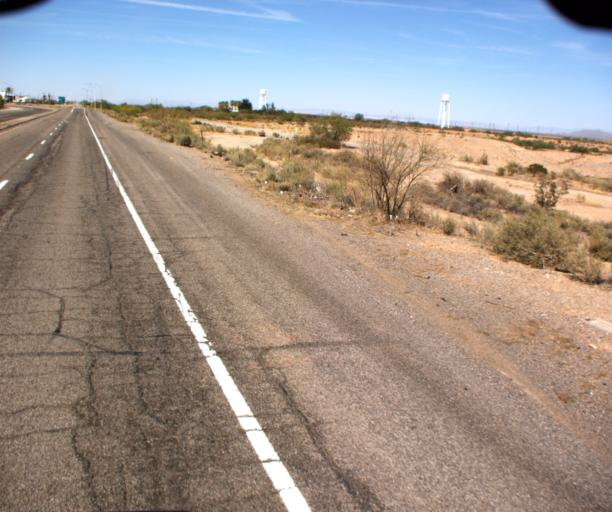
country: US
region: Arizona
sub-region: Pinal County
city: Eloy
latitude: 32.7295
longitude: -111.5158
